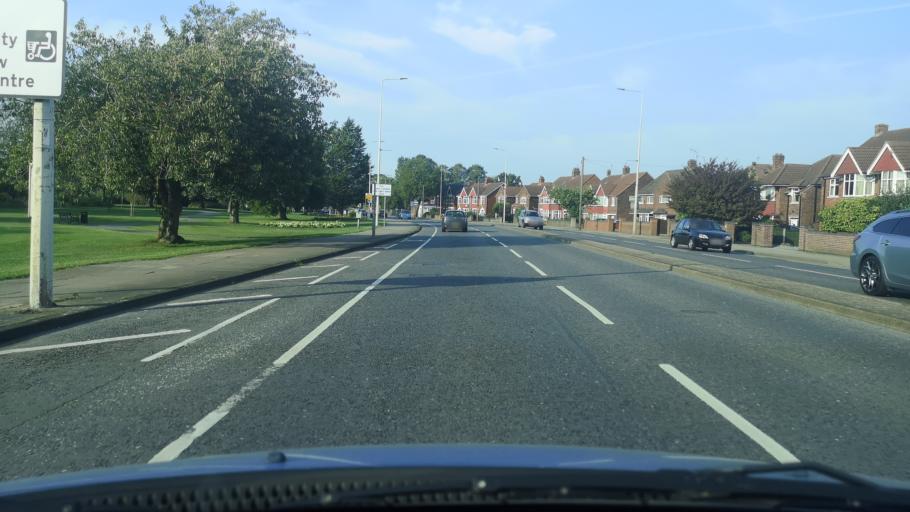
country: GB
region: England
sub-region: North Lincolnshire
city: Scunthorpe
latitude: 53.5821
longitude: -0.6537
